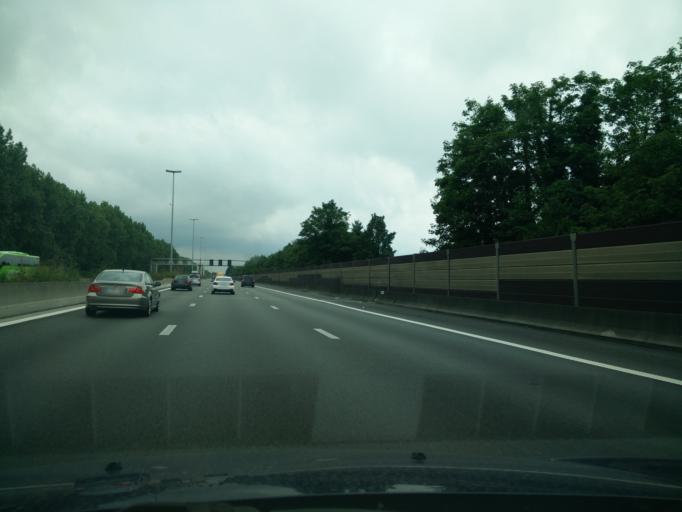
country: BE
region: Flanders
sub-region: Provincie Oost-Vlaanderen
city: Merelbeke
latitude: 51.0019
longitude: 3.7195
